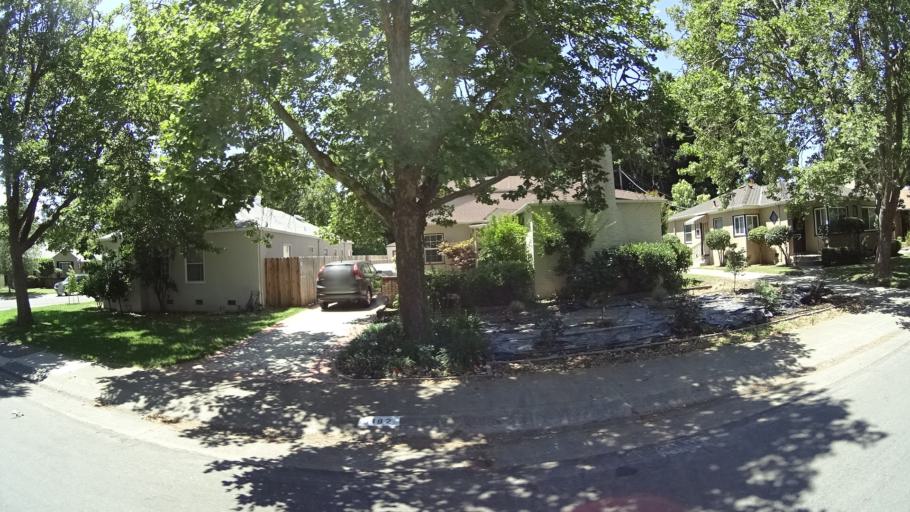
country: US
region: California
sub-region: Sacramento County
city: Sacramento
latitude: 38.5442
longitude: -121.5058
